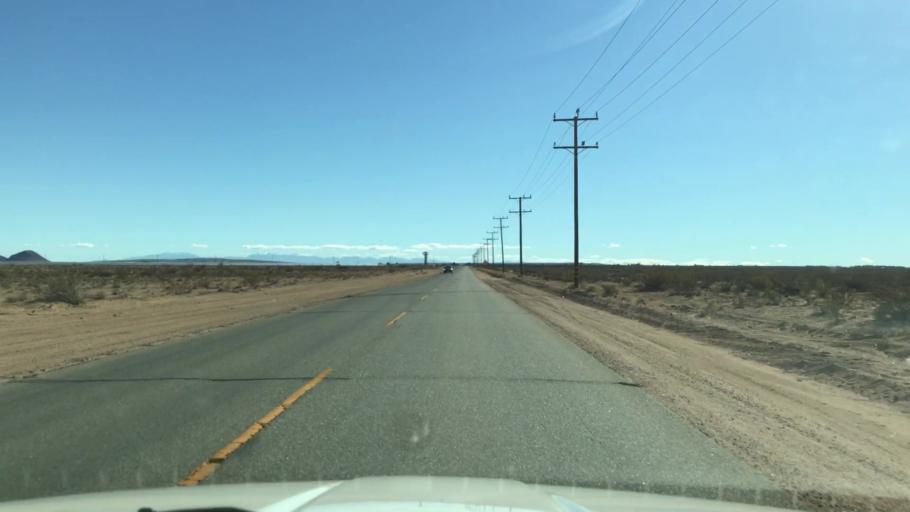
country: US
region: California
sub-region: Kern County
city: California City
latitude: 35.1639
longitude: -117.9858
